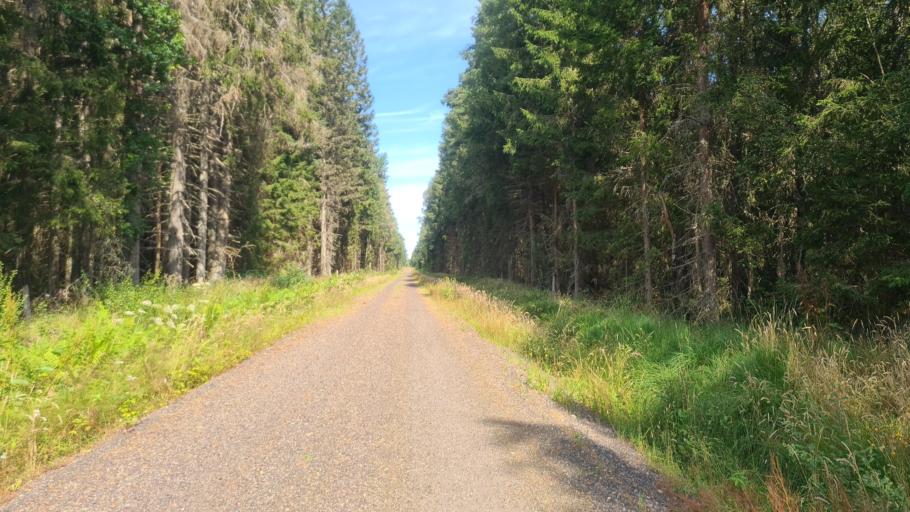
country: SE
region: Kronoberg
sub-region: Ljungby Kommun
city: Lagan
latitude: 56.9760
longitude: 13.9482
